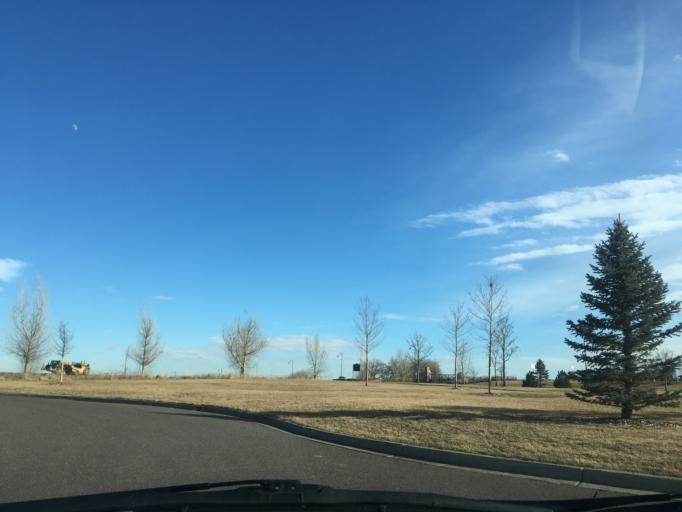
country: US
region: Colorado
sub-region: Boulder County
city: Lafayette
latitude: 39.9813
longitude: -105.0249
